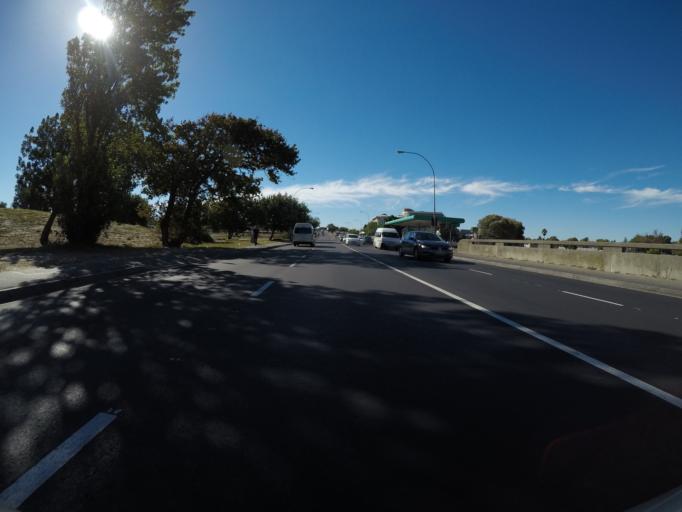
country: ZA
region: Western Cape
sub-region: City of Cape Town
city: Kraaifontein
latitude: -33.9209
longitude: 18.6757
